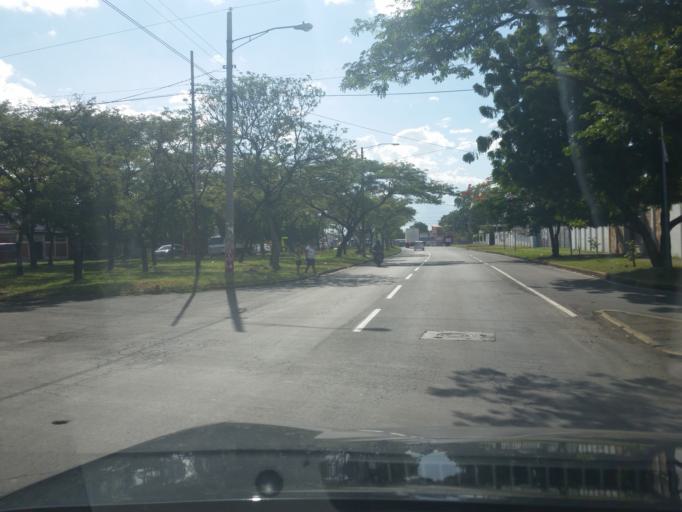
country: NI
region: Managua
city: Managua
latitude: 12.1556
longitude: -86.2852
